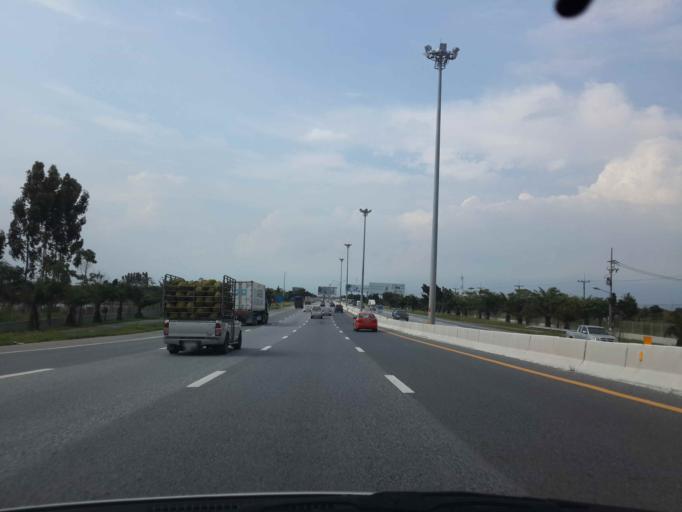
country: TH
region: Chon Buri
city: Phan Thong
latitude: 13.4821
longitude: 101.0464
